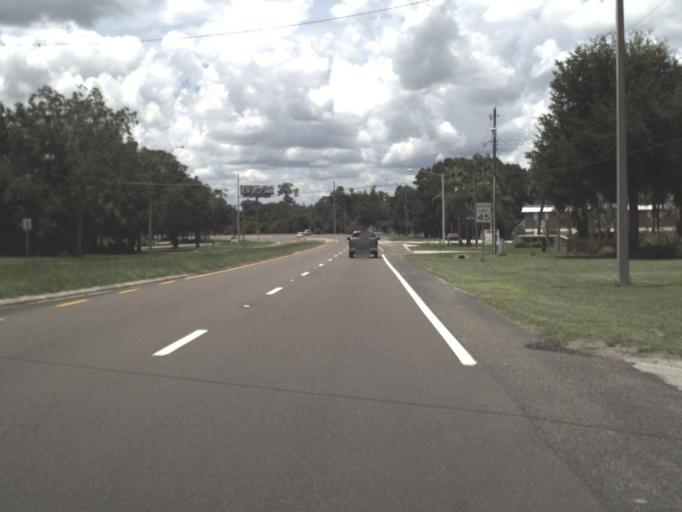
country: US
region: Florida
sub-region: Hillsborough County
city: Plant City
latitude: 28.0209
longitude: -82.1447
